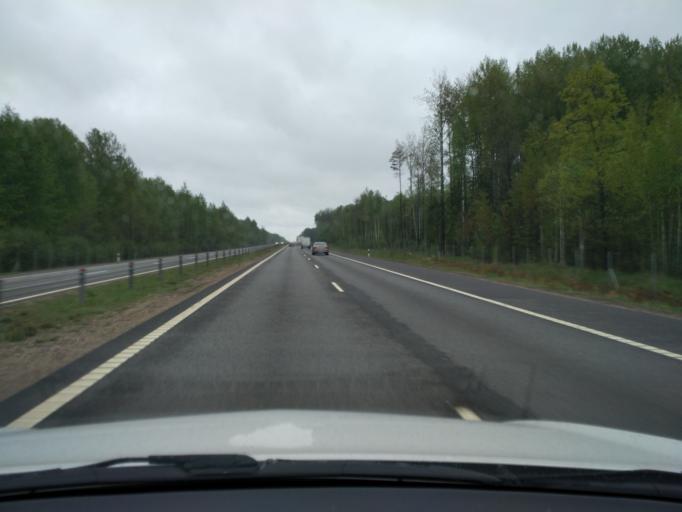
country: BY
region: Mogilev
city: Asipovichy
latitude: 53.2917
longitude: 28.8123
